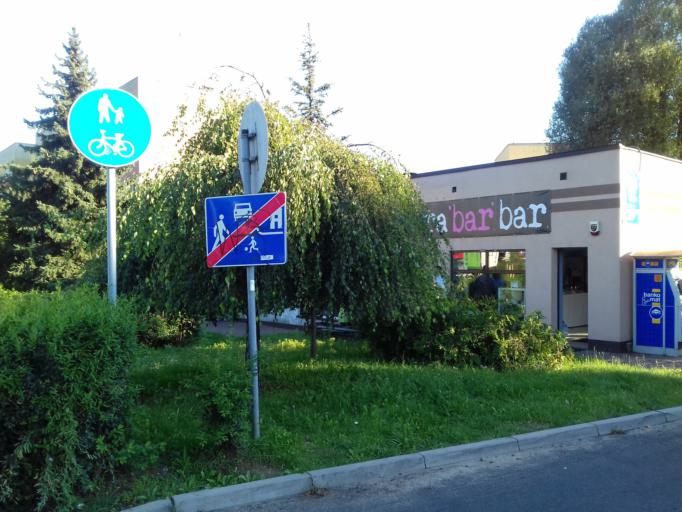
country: PL
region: Silesian Voivodeship
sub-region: Czestochowa
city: Czestochowa
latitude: 50.8424
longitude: 19.1286
